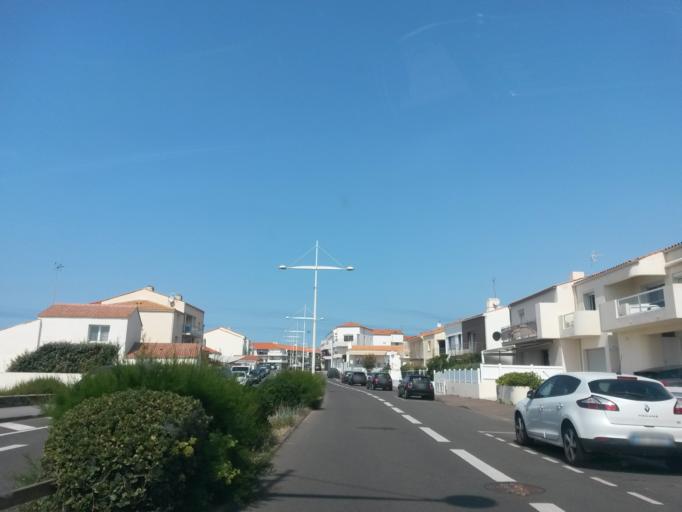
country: FR
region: Pays de la Loire
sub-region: Departement de la Vendee
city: Les Sables-d'Olonne
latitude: 46.4928
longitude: -1.8098
